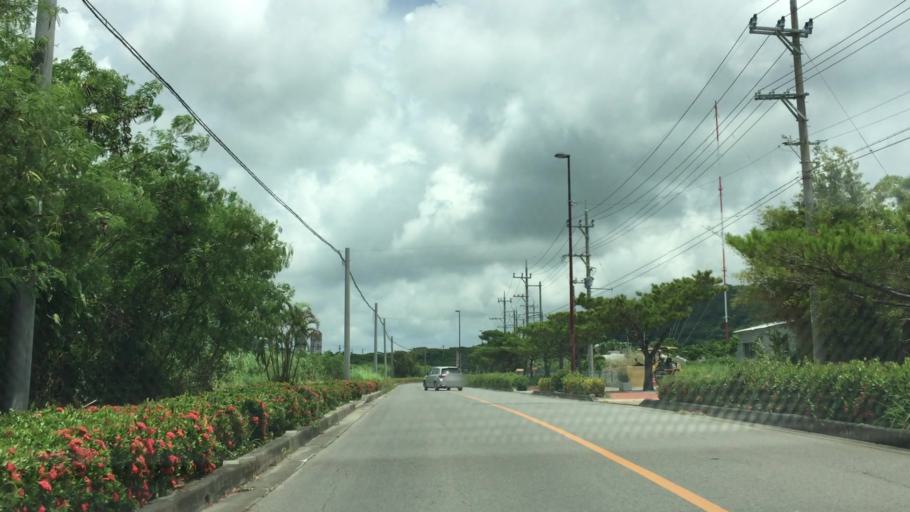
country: JP
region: Okinawa
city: Ishigaki
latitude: 24.3606
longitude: 124.1570
